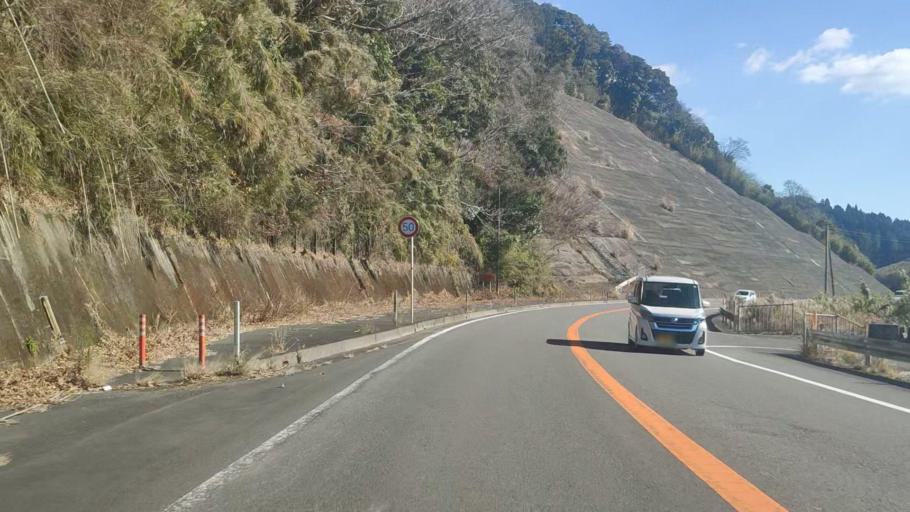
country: JP
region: Kagoshima
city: Sueyoshicho-ninokata
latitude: 31.6616
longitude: 130.8933
